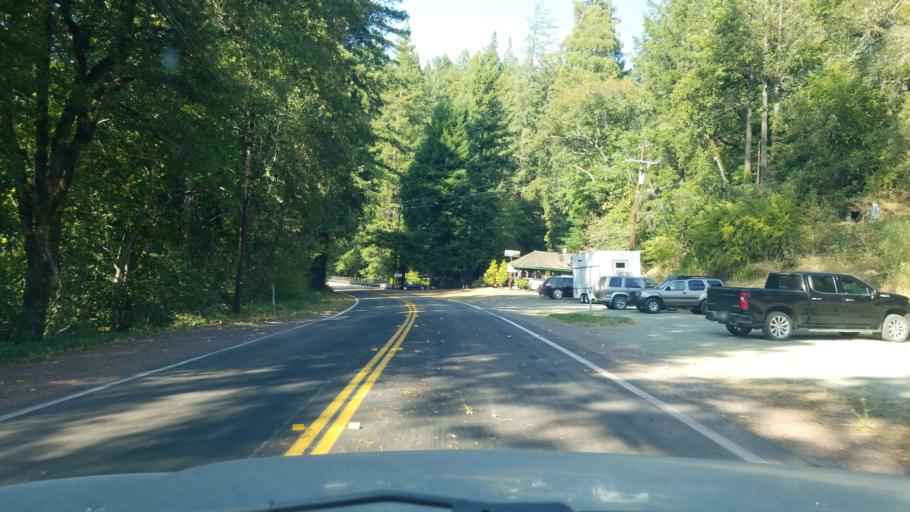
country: US
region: California
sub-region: Humboldt County
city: Redway
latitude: 40.1916
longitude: -123.7686
